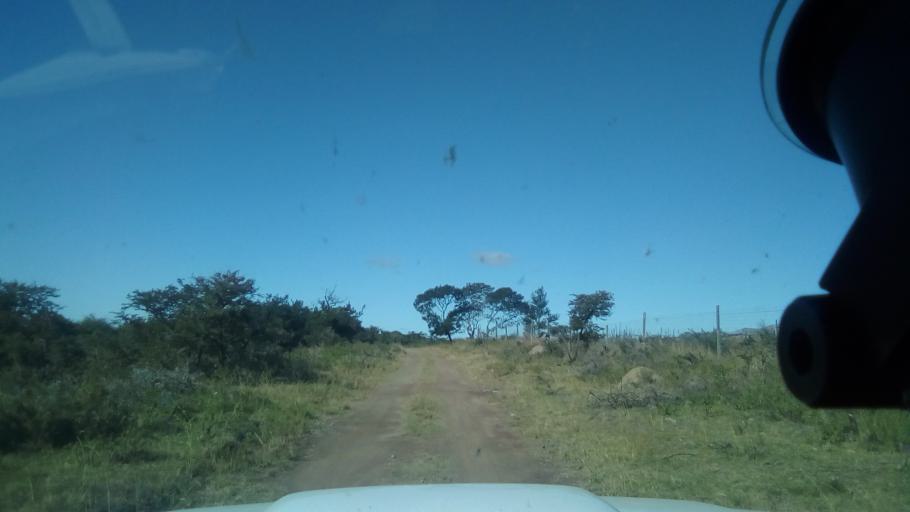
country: ZA
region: Eastern Cape
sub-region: Buffalo City Metropolitan Municipality
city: Bhisho
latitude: -32.7781
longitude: 27.3370
